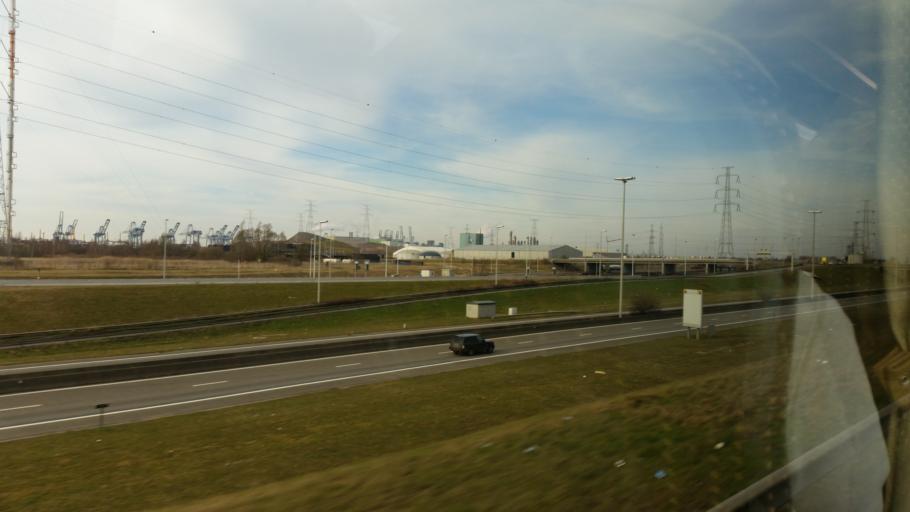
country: BE
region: Flanders
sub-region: Provincie Oost-Vlaanderen
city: Beveren
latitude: 51.2741
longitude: 4.2808
